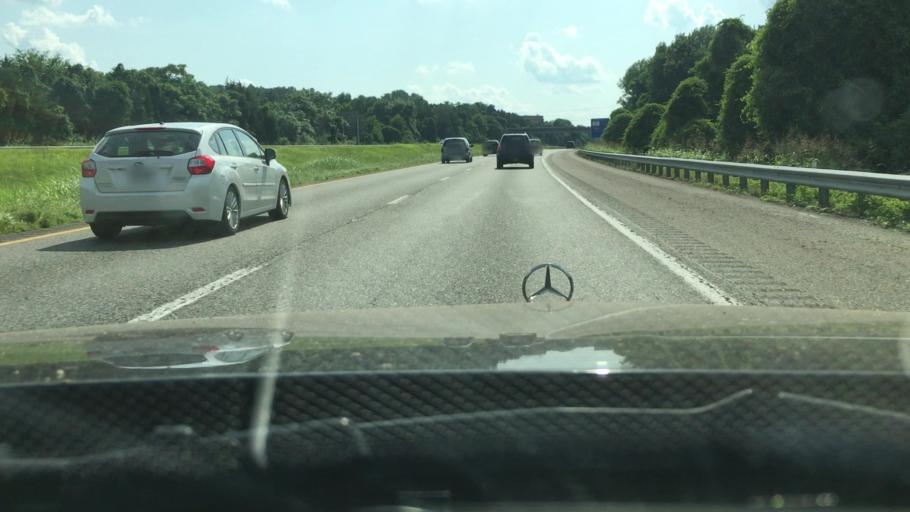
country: US
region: Virginia
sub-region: City of Charlottesville
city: Charlottesville
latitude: 38.0080
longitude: -78.4885
